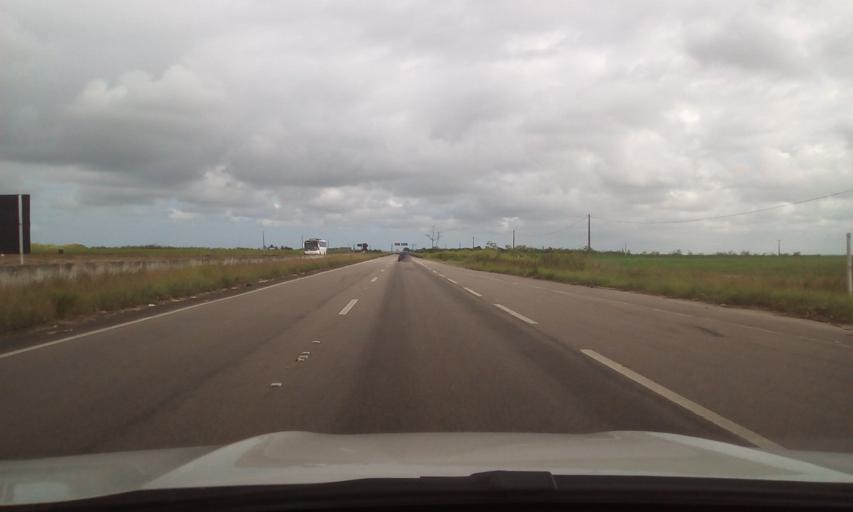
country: BR
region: Pernambuco
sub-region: Itapissuma
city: Itapissuma
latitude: -7.6682
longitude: -34.9333
